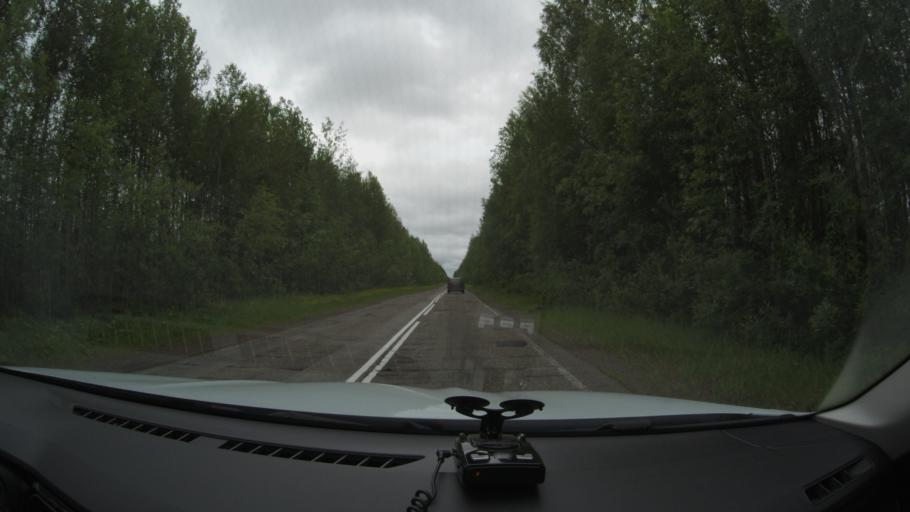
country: RU
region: Komi Republic
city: Sosnogorsk
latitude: 63.6027
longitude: 54.3498
